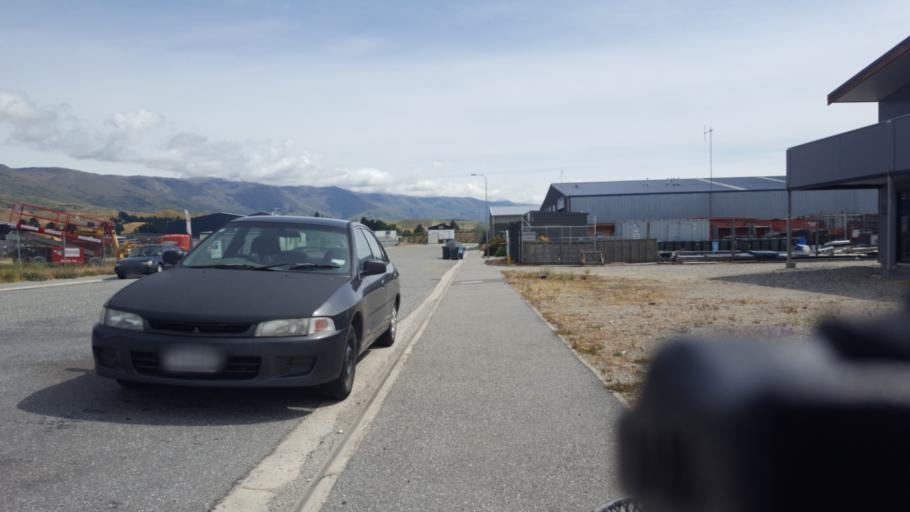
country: NZ
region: Otago
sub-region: Queenstown-Lakes District
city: Wanaka
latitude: -45.0511
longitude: 169.1916
